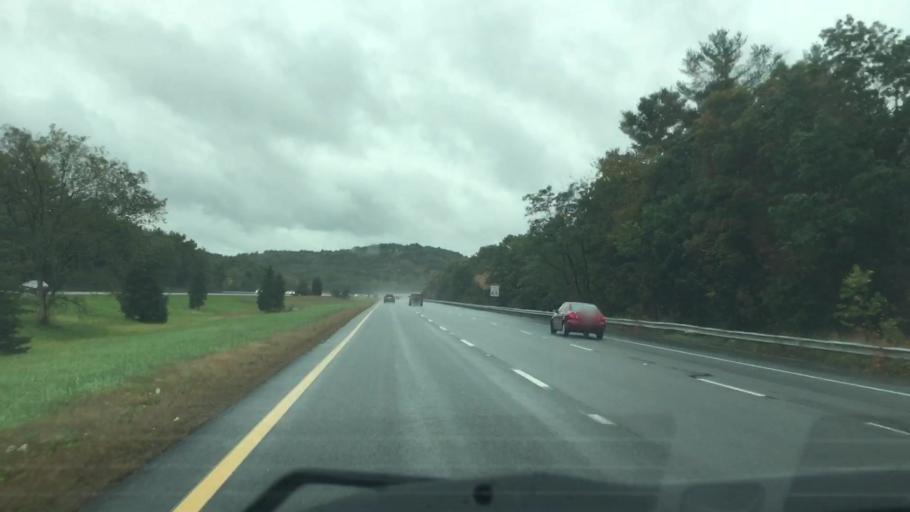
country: US
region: Massachusetts
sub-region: Essex County
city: Merrimac
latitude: 42.8128
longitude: -71.0264
